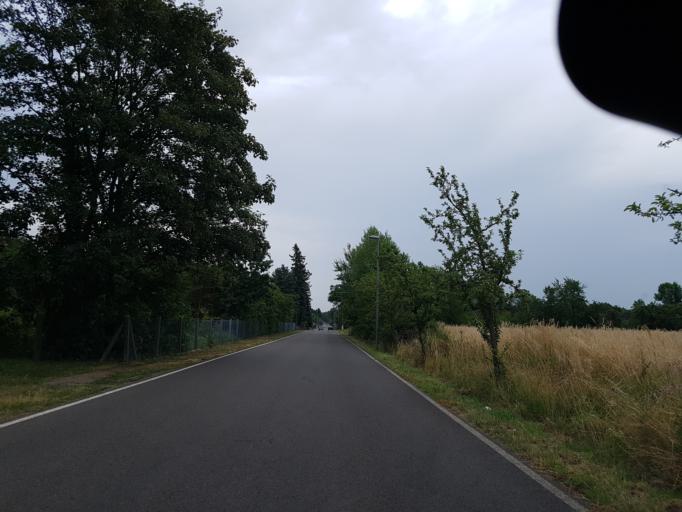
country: DE
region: Brandenburg
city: Schipkau
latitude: 51.5522
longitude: 13.9182
